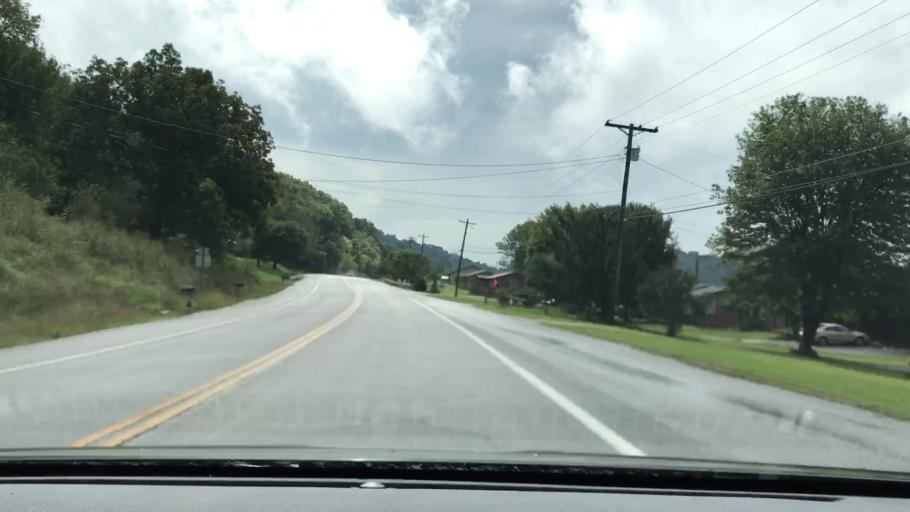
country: US
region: Tennessee
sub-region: Smith County
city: Carthage
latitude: 36.3162
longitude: -85.9701
